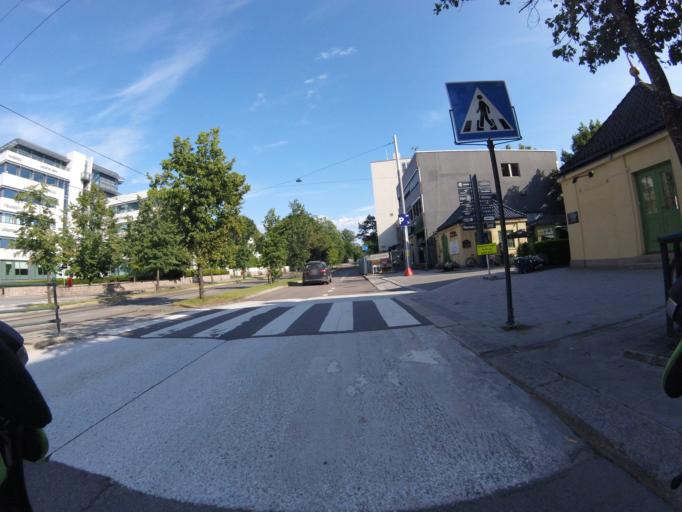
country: NO
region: Oslo
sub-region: Oslo
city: Sjolyststranda
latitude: 59.9216
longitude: 10.6880
